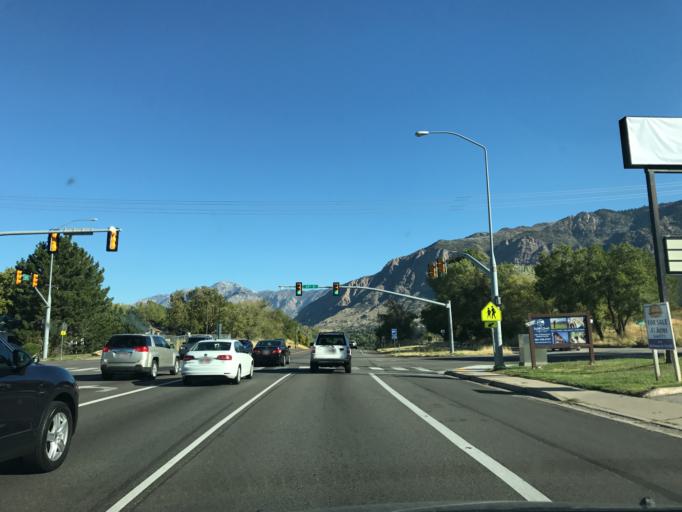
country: US
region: Utah
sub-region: Weber County
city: Ogden
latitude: 41.2305
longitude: -111.9479
